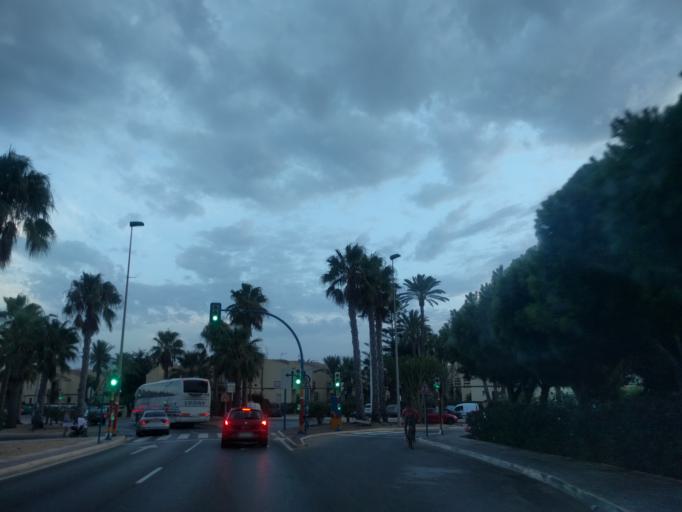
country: ES
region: Murcia
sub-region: Murcia
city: La Manga del Mar Menor
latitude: 37.6634
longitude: -0.7291
